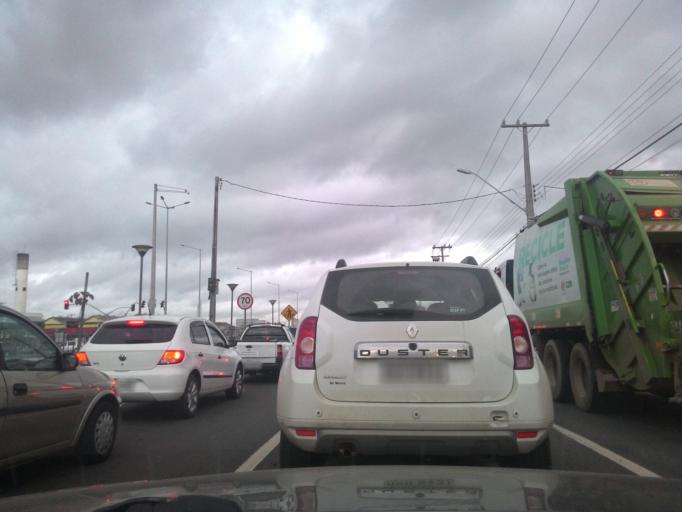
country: BR
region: Parana
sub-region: Curitiba
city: Curitiba
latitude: -25.4749
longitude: -49.2582
